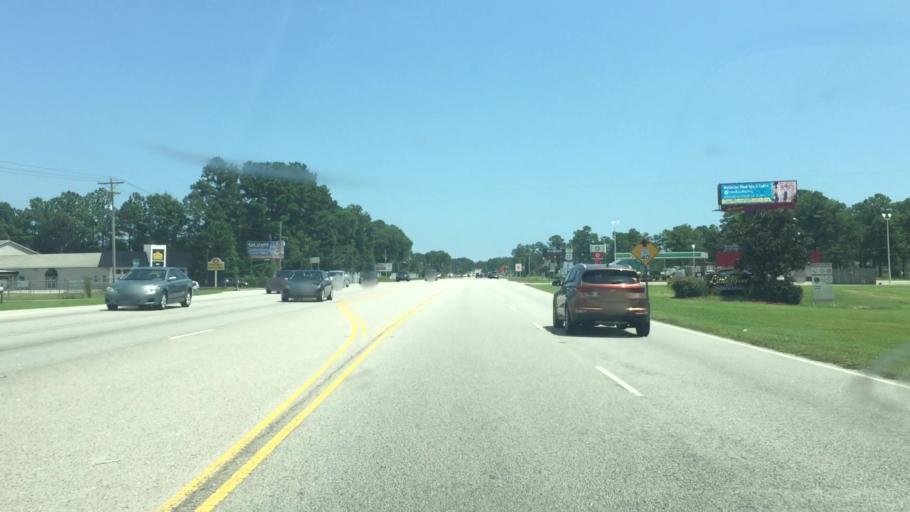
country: US
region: South Carolina
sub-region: Horry County
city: North Myrtle Beach
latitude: 33.8717
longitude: -78.6728
